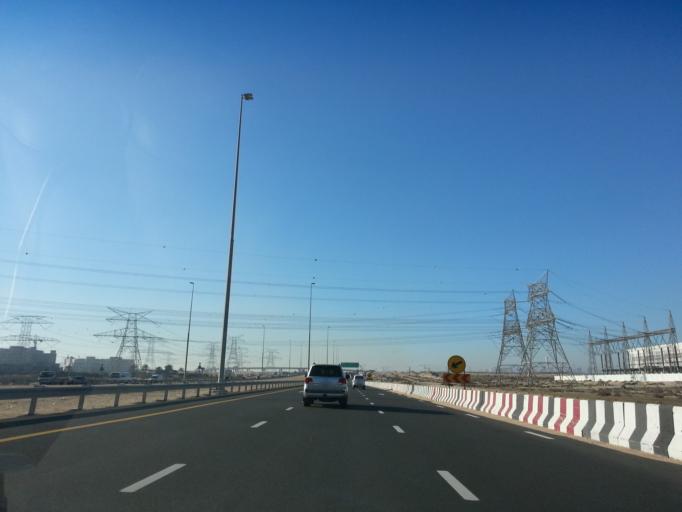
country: AE
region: Dubai
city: Dubai
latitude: 25.0079
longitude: 55.1702
